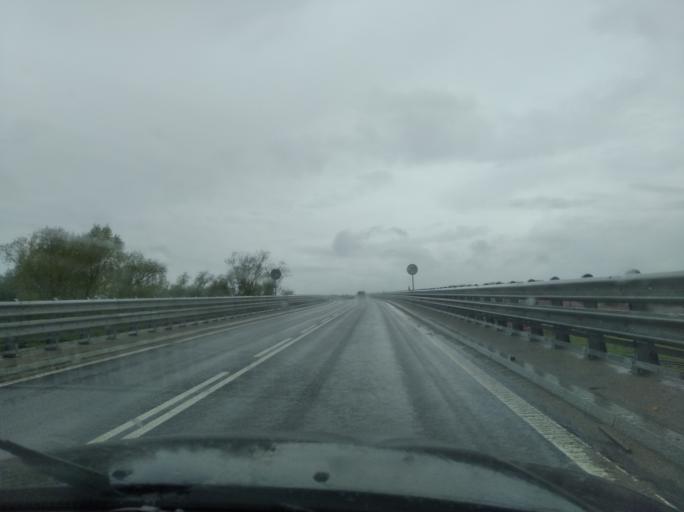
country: PL
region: Subcarpathian Voivodeship
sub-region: Powiat strzyzowski
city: Czudec
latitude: 49.9382
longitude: 21.8253
